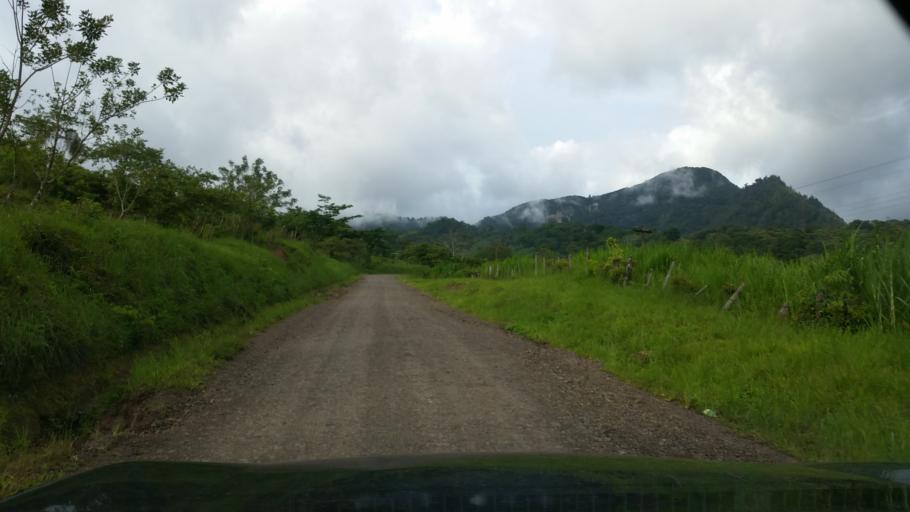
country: NI
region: Jinotega
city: Jinotega
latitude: 13.2602
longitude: -85.7379
